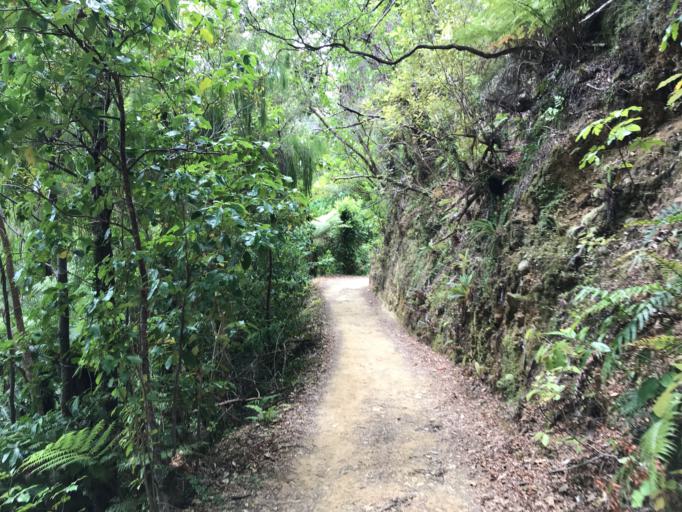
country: NZ
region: Marlborough
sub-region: Marlborough District
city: Picton
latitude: -41.0964
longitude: 174.1884
